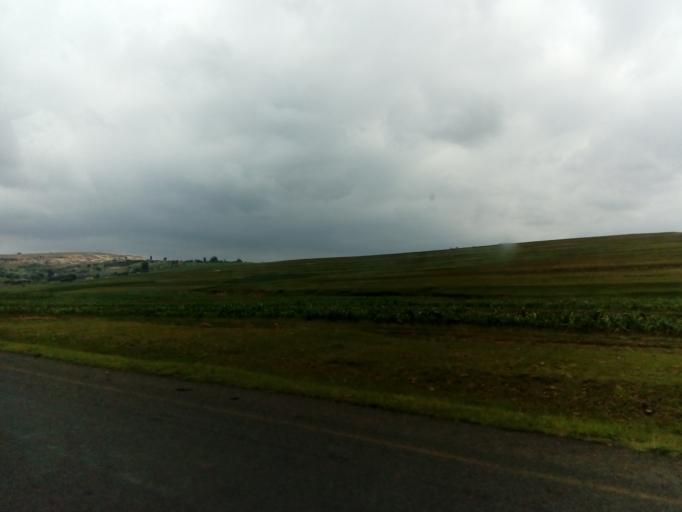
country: LS
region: Leribe
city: Leribe
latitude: -29.0015
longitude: 27.9904
